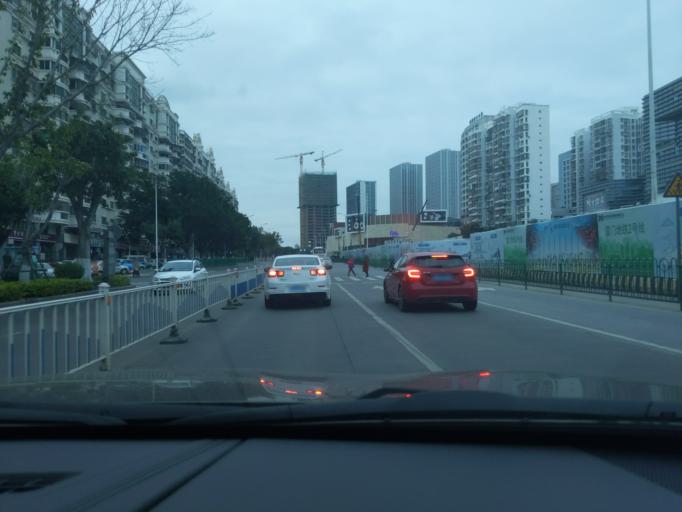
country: CN
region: Fujian
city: Liuwudian
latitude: 24.4858
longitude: 118.1728
